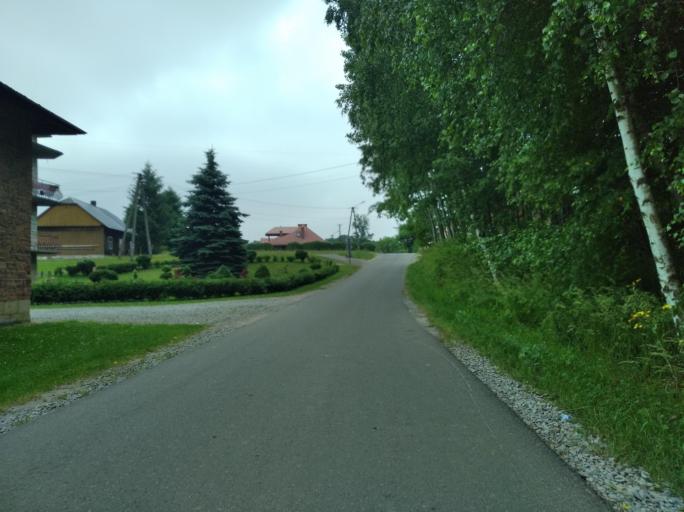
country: PL
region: Subcarpathian Voivodeship
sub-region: Powiat brzozowski
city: Haczow
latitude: 49.6747
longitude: 21.8926
